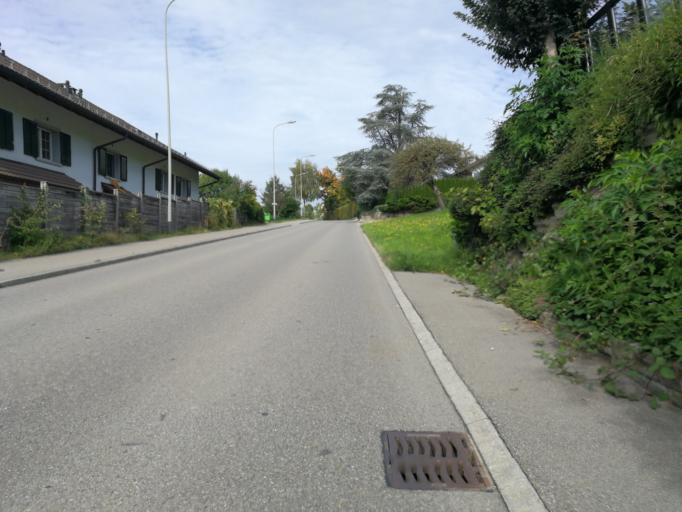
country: CH
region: Zurich
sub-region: Bezirk Meilen
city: Mannedorf
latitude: 47.2549
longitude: 8.7073
